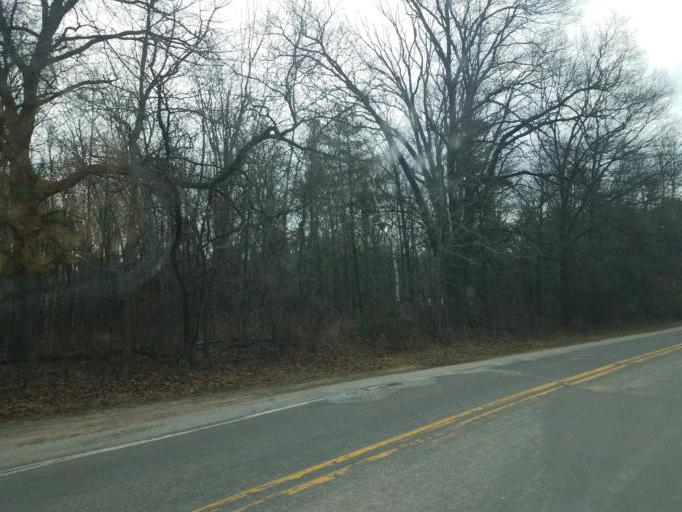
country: US
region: Michigan
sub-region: Oceana County
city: Hart
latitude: 43.6575
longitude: -86.5230
